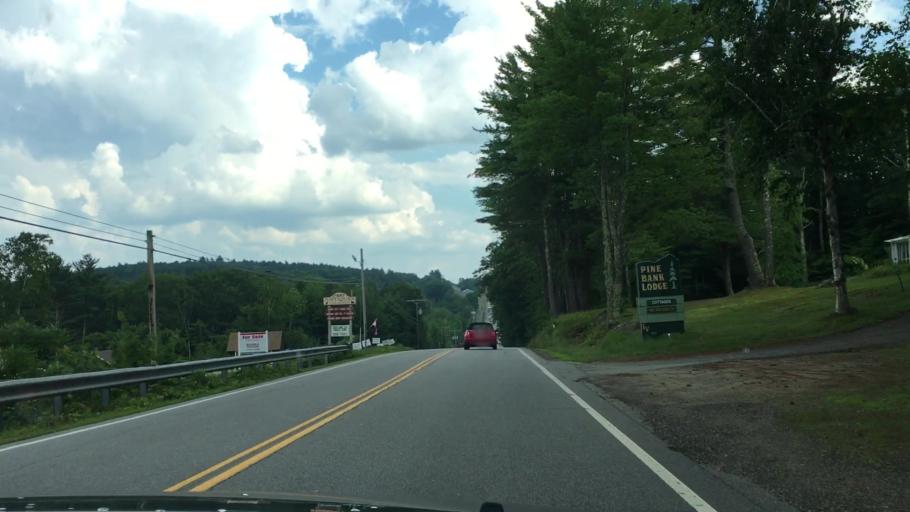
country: US
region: New Hampshire
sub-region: Belknap County
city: Meredith
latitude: 43.6218
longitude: -71.4847
